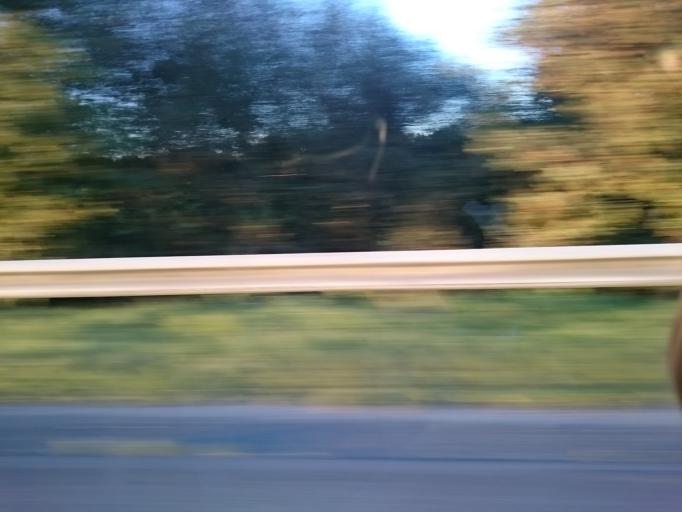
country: FR
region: Brittany
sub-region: Departement du Finistere
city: Lampaul-Guimiliau
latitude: 48.5199
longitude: -4.0130
